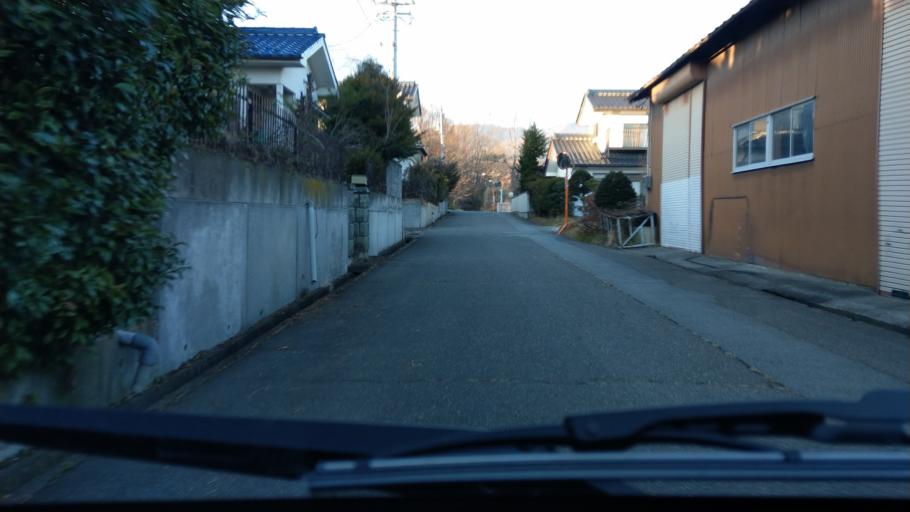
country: JP
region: Nagano
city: Komoro
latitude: 36.3181
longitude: 138.4559
